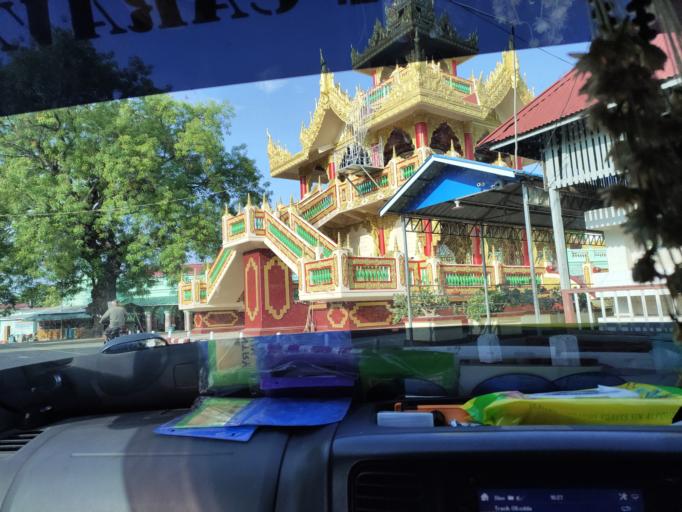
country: MM
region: Magway
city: Magway
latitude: 20.1700
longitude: 94.9186
